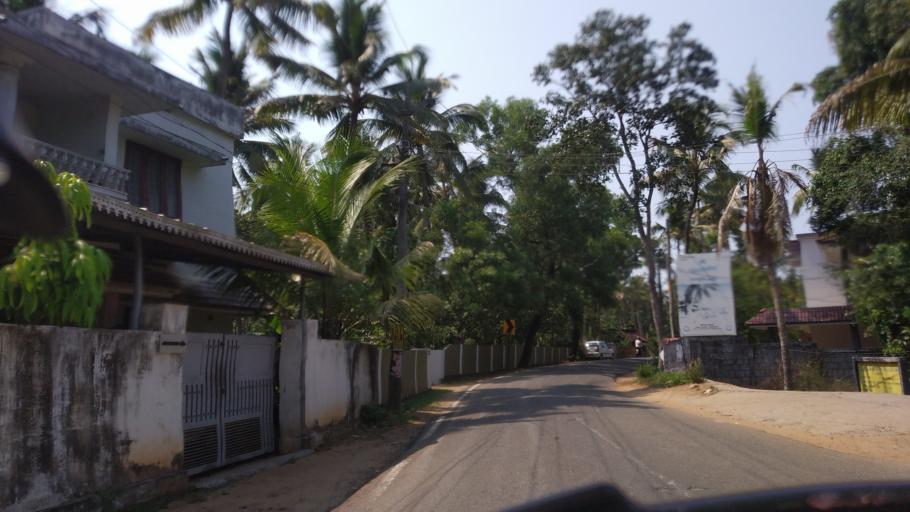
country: IN
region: Kerala
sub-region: Thrissur District
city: Irinjalakuda
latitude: 10.2985
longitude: 76.1324
